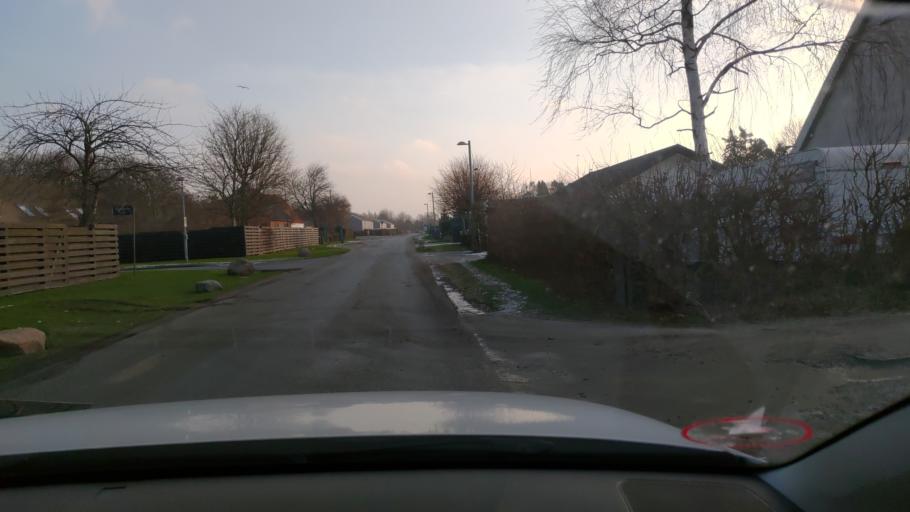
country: DK
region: Zealand
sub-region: Solrod Kommune
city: Solrod Strand
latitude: 55.5431
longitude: 12.2213
